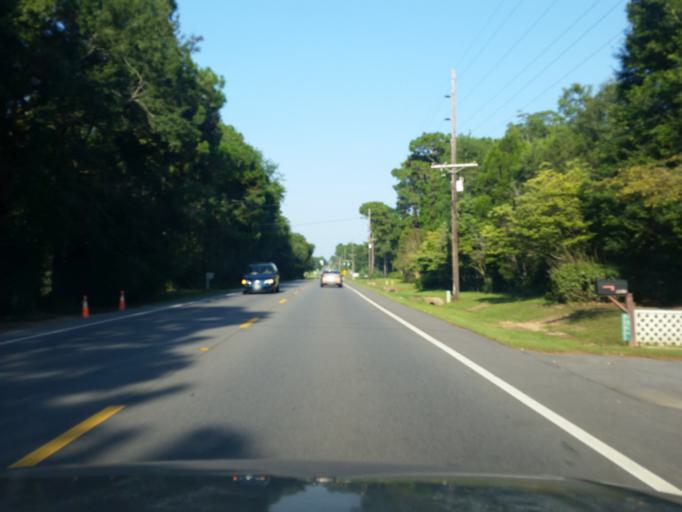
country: US
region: Alabama
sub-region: Baldwin County
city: Elberta
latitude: 30.4068
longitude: -87.6362
